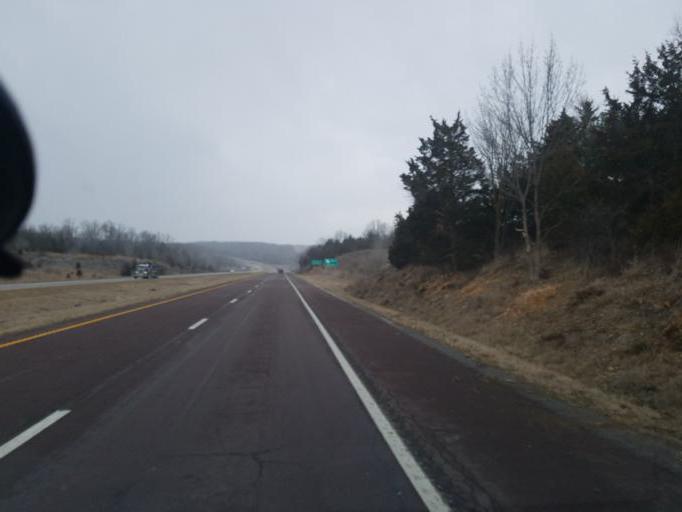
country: US
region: Missouri
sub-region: Boone County
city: Hallsville
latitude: 39.1350
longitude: -92.3327
